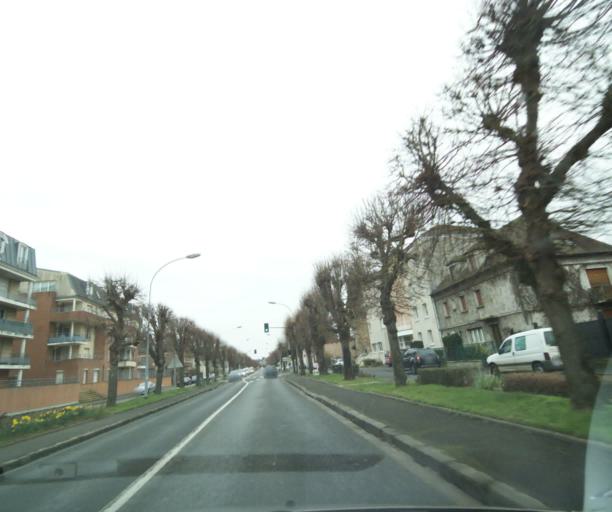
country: FR
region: Picardie
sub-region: Departement de l'Oise
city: Noyon
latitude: 49.5778
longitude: 2.9970
